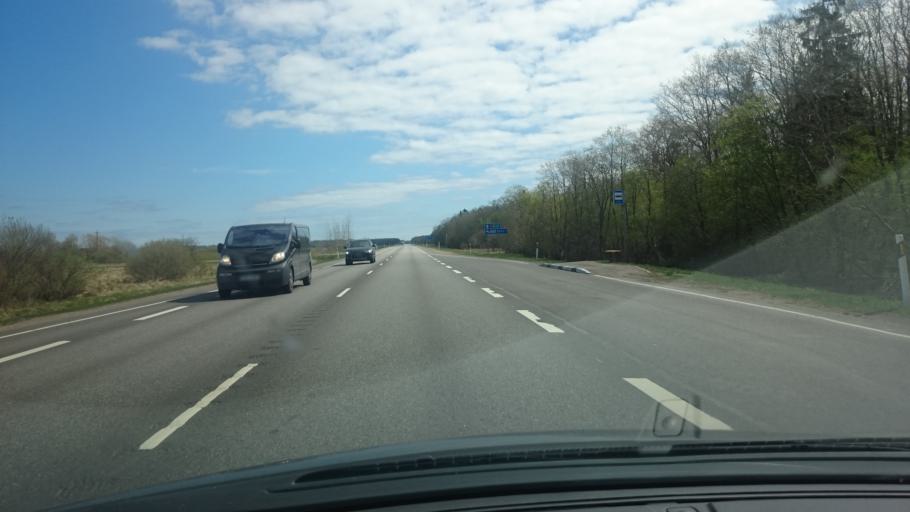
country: EE
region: Ida-Virumaa
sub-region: Kohtla-Jaerve linn
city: Kohtla-Jarve
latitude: 59.4210
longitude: 27.2147
